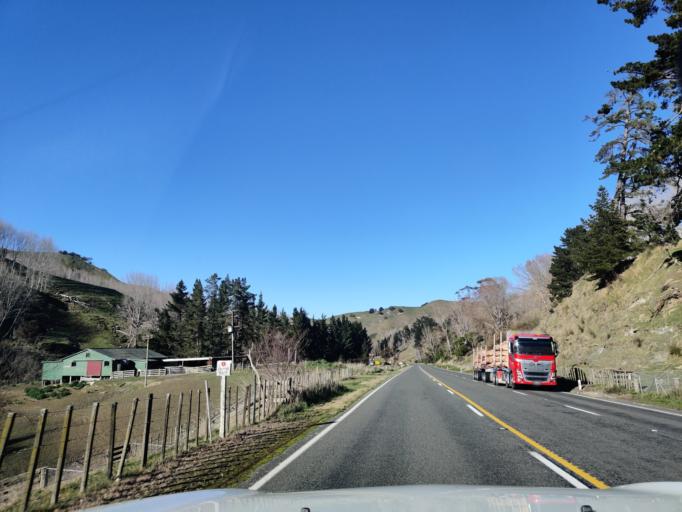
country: NZ
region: Manawatu-Wanganui
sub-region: Ruapehu District
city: Waiouru
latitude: -39.7861
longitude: 175.7858
